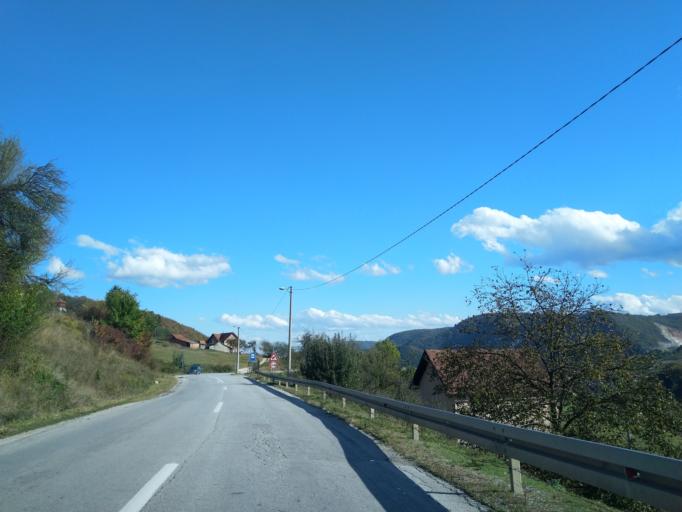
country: RS
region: Central Serbia
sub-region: Zlatiborski Okrug
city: Uzice
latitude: 43.8663
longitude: 19.8055
